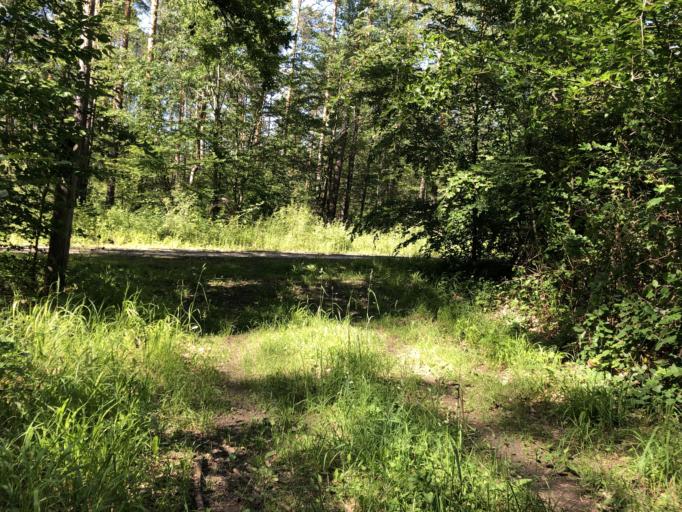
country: DE
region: Bavaria
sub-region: Upper Franconia
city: Memmelsdorf
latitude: 49.9112
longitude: 10.9600
